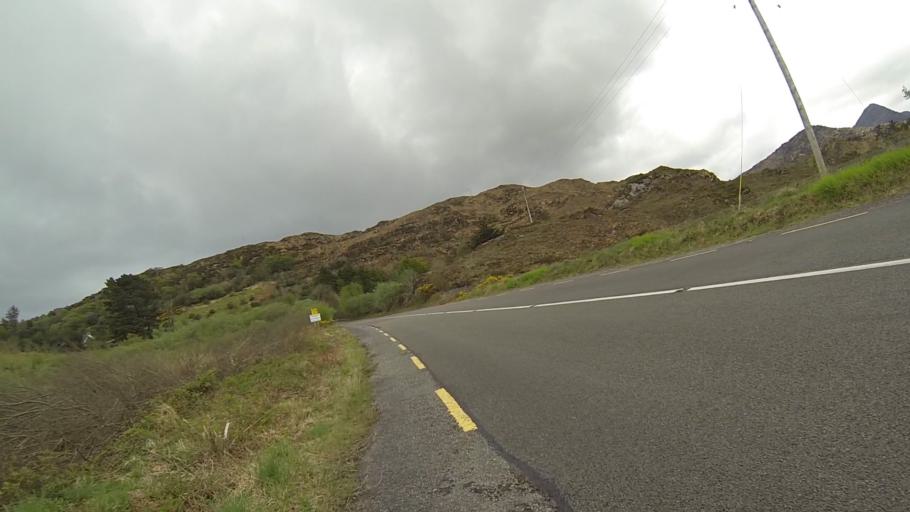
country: IE
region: Munster
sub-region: County Cork
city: Bantry
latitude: 51.7210
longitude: -9.5804
